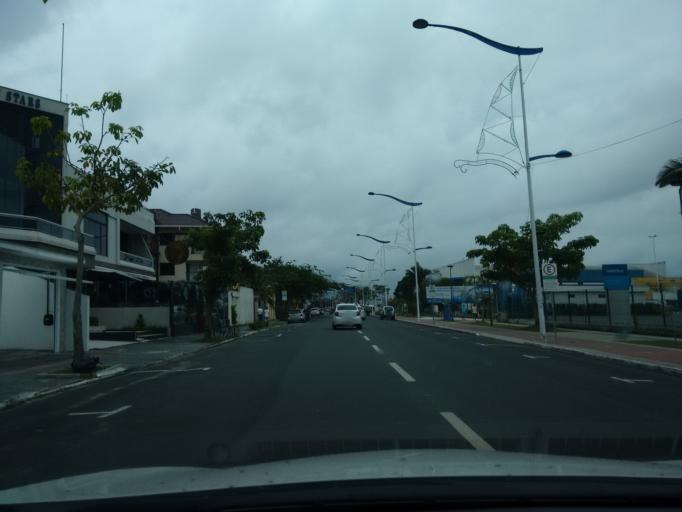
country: BR
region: Santa Catarina
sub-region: Itajai
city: Itajai
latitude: -26.9118
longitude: -48.6537
